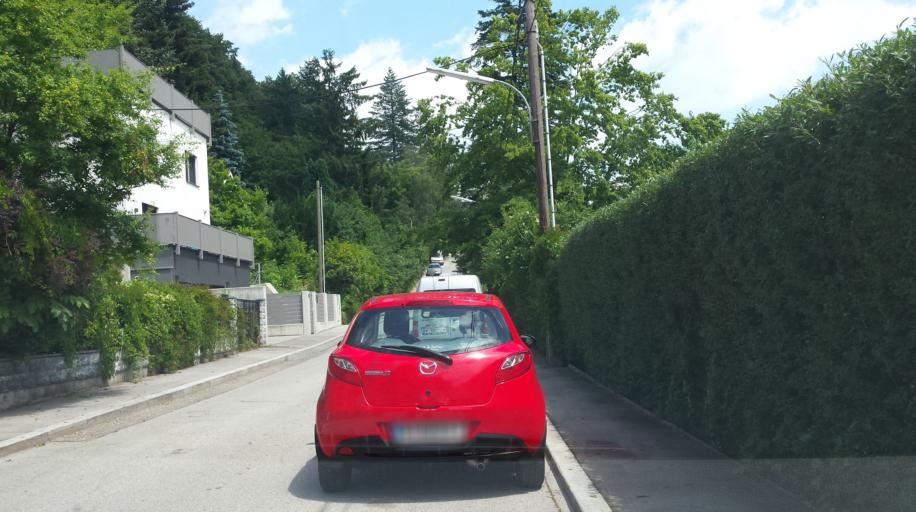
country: AT
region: Lower Austria
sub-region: Politischer Bezirk Wien-Umgebung
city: Mauerbach
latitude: 48.2472
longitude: 16.2157
